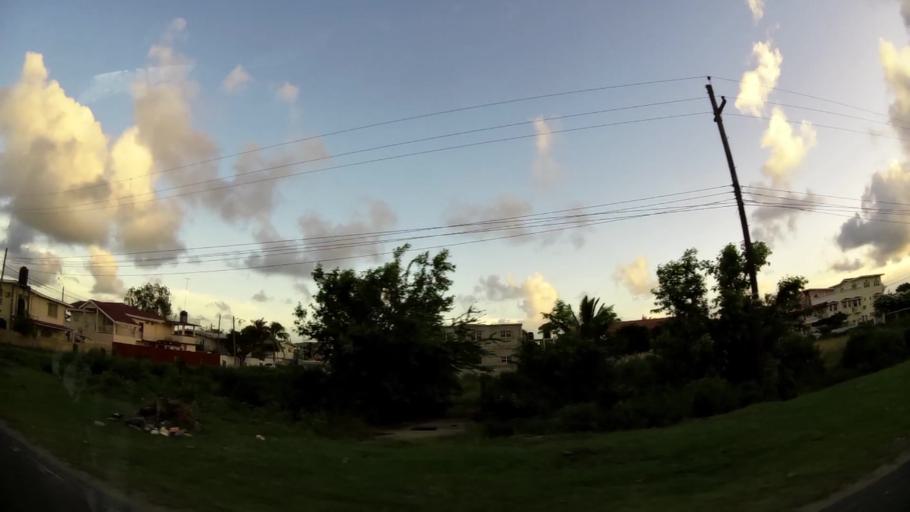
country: GY
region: Demerara-Mahaica
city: Georgetown
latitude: 6.8138
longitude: -58.1000
